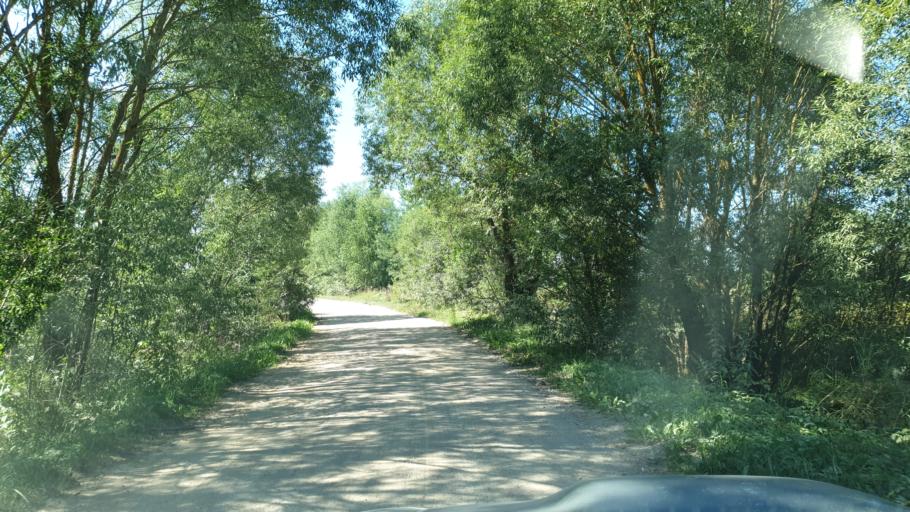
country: LT
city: Sirvintos
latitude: 54.9165
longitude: 24.9151
